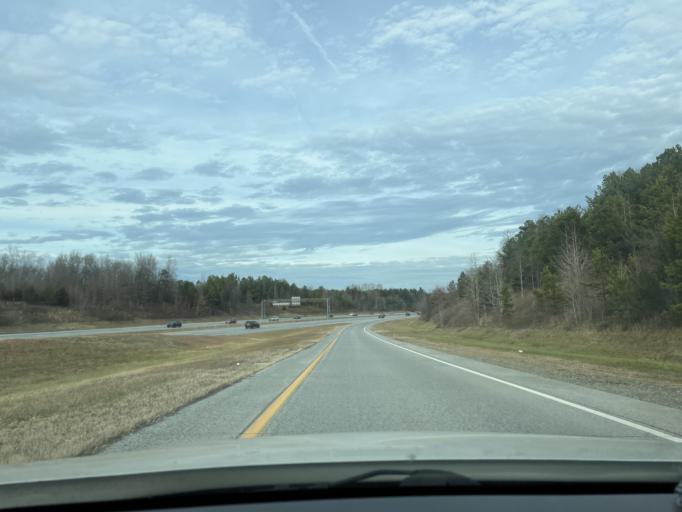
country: US
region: North Carolina
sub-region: Guilford County
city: Forest Oaks
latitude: 36.0247
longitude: -79.7276
